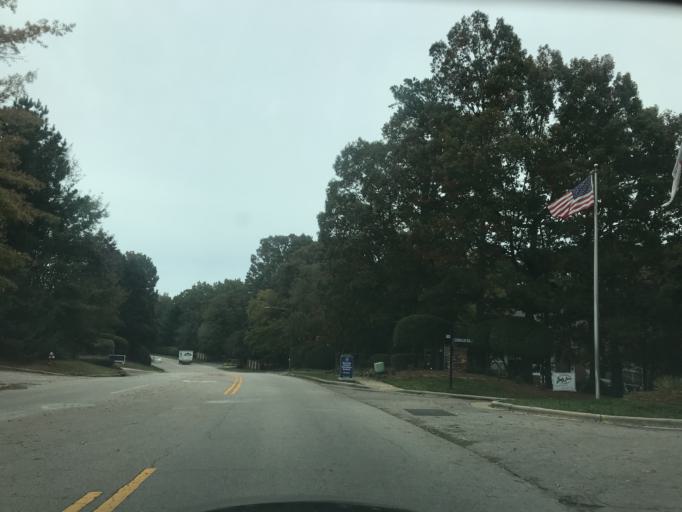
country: US
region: North Carolina
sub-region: Wake County
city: West Raleigh
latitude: 35.8898
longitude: -78.6771
